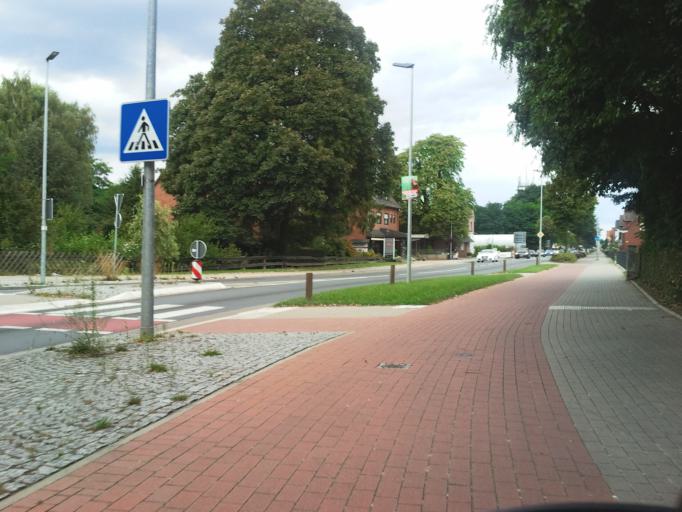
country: DE
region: Lower Saxony
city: Nienburg
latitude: 52.6560
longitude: 9.2194
